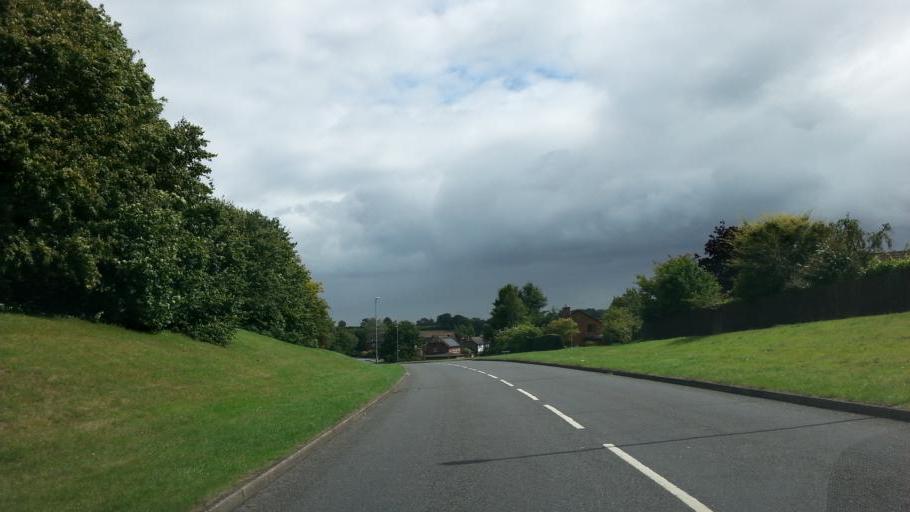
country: GB
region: England
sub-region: Northamptonshire
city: Earls Barton
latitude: 52.2656
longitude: -0.8103
